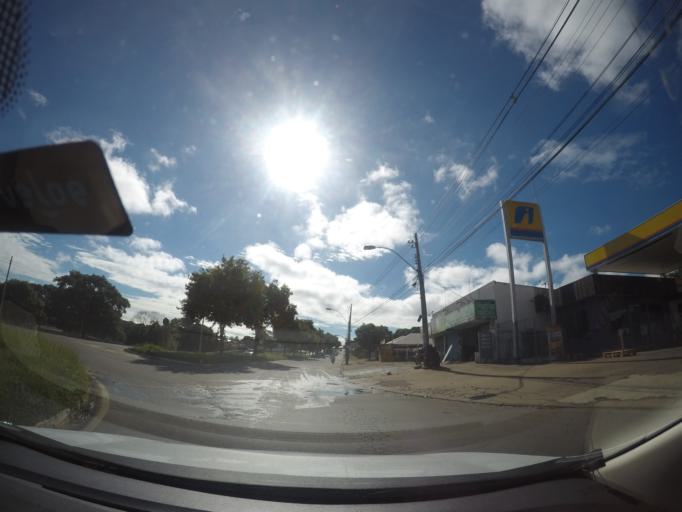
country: BR
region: Goias
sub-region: Goiania
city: Goiania
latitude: -16.6590
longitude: -49.1919
